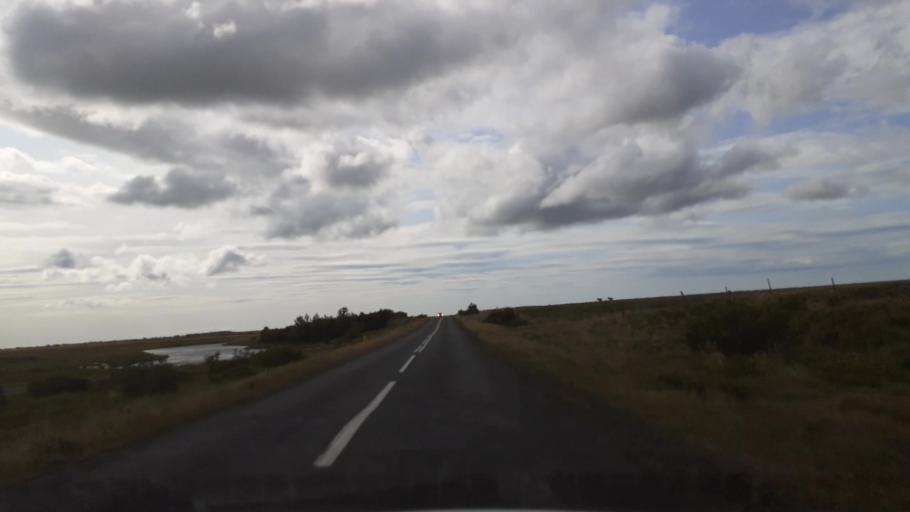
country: IS
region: South
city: Vestmannaeyjar
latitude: 63.8302
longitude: -20.4240
